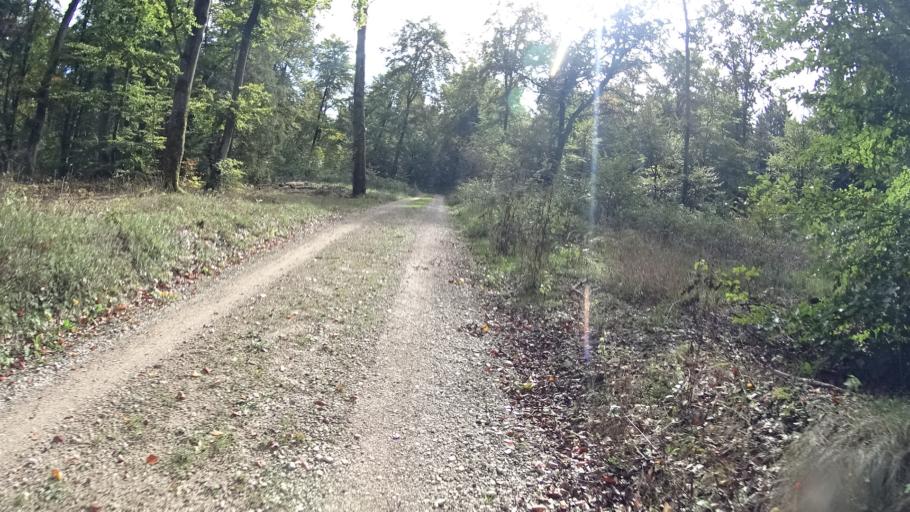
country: DE
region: Bavaria
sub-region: Upper Bavaria
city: Walting
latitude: 48.9013
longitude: 11.3009
